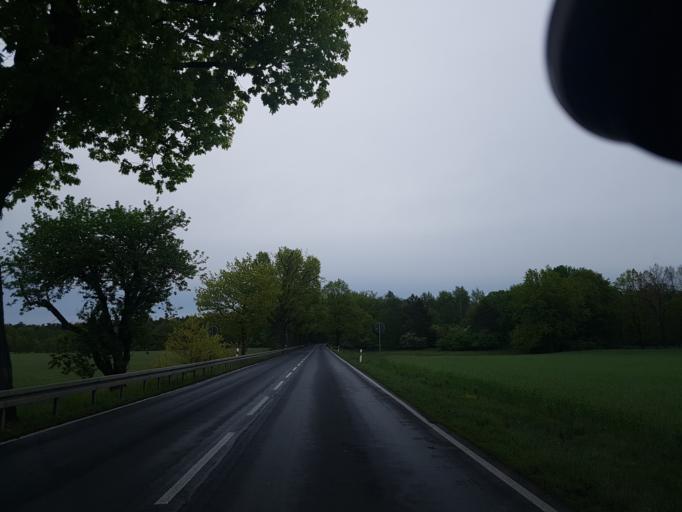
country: DE
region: Brandenburg
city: Neupetershain
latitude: 51.6267
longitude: 14.1701
